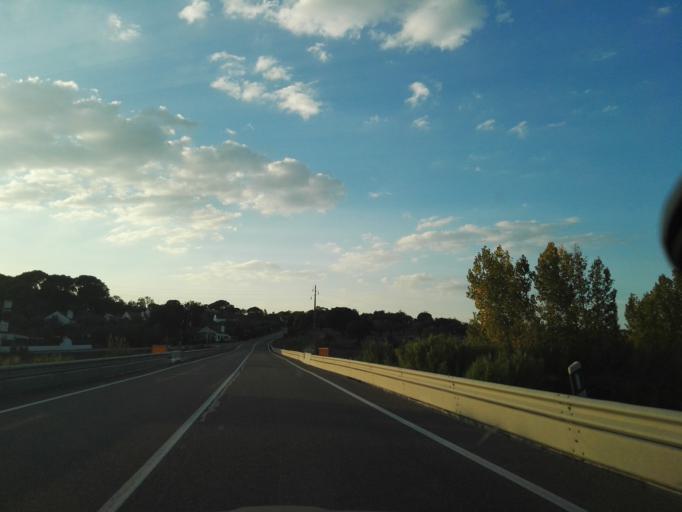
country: PT
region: Evora
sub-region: Mora
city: Mora
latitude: 38.9415
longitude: -8.1305
